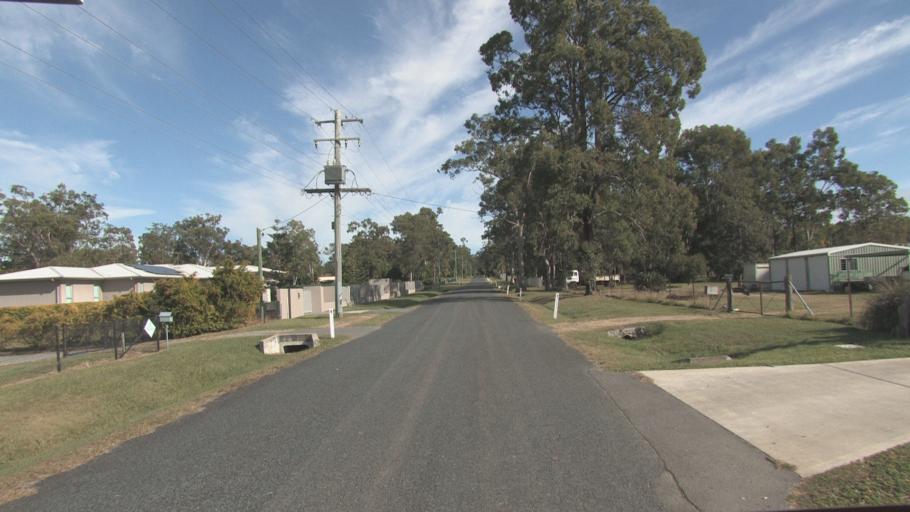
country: AU
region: Queensland
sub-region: Brisbane
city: Forest Lake
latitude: -27.6581
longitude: 152.9886
